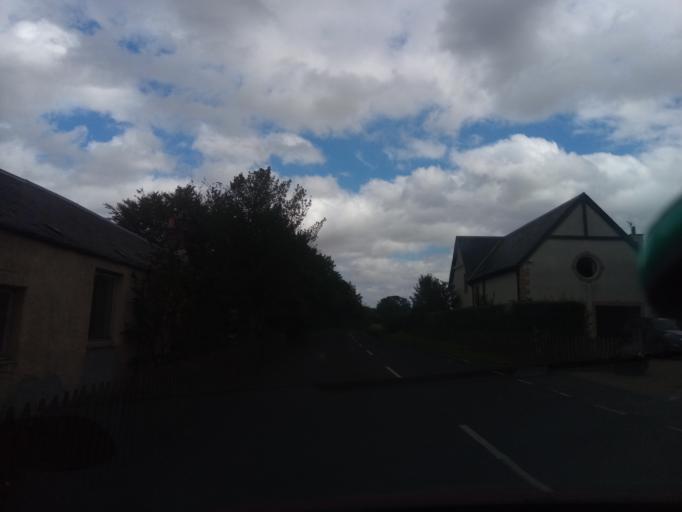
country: GB
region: Scotland
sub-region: The Scottish Borders
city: Kelso
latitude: 55.6000
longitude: -2.4182
